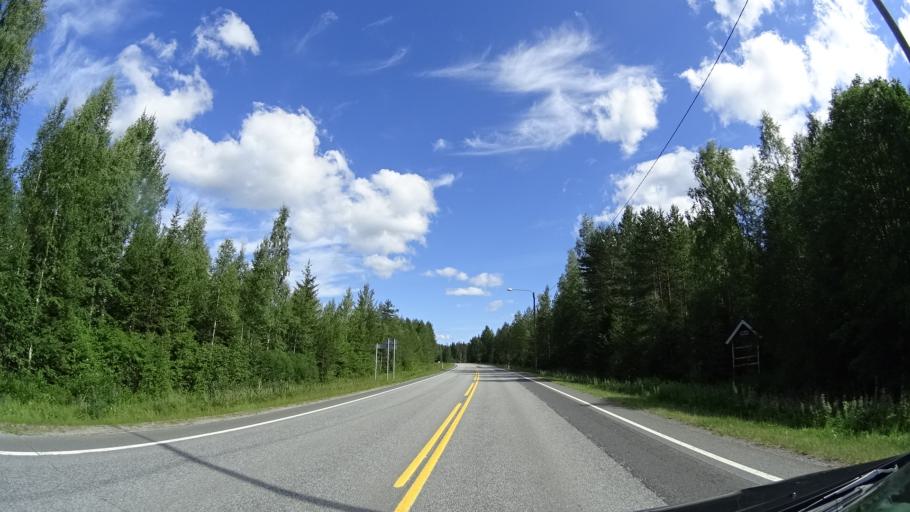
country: FI
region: Pirkanmaa
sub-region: Luoteis-Pirkanmaa
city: Kihnioe
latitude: 62.1771
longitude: 23.1712
